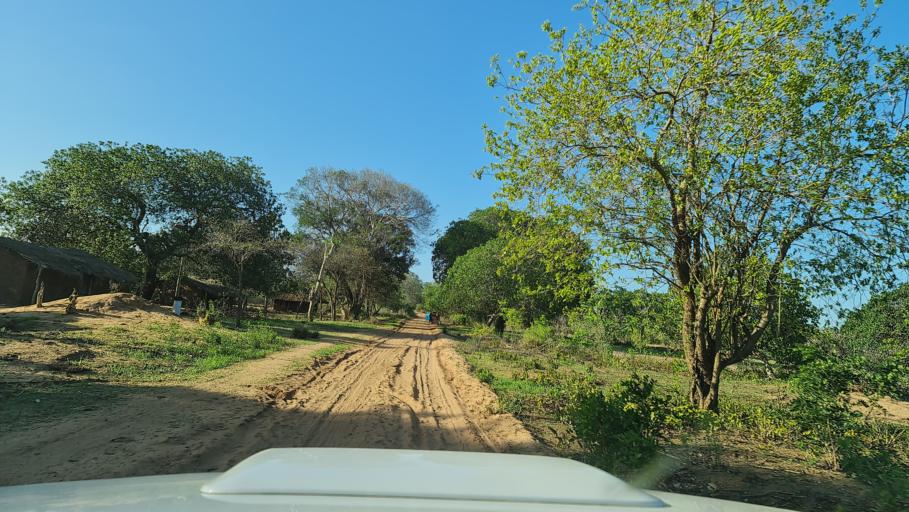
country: MZ
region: Nampula
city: Nacala
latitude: -14.6996
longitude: 40.3271
